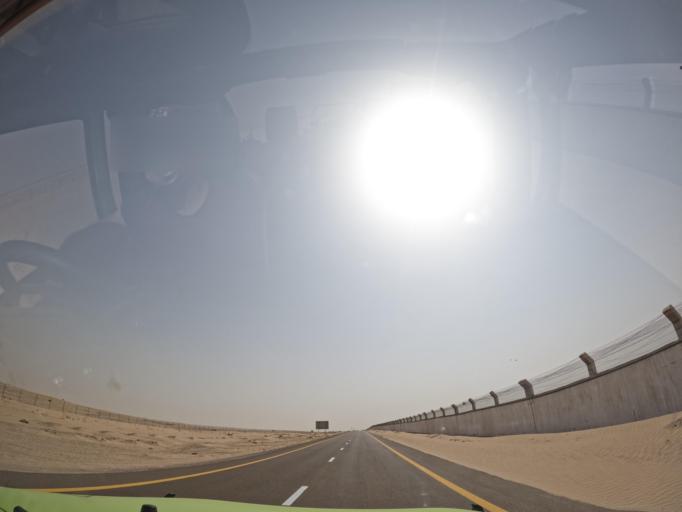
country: AE
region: Dubai
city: Dubai
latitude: 24.6167
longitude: 55.3356
